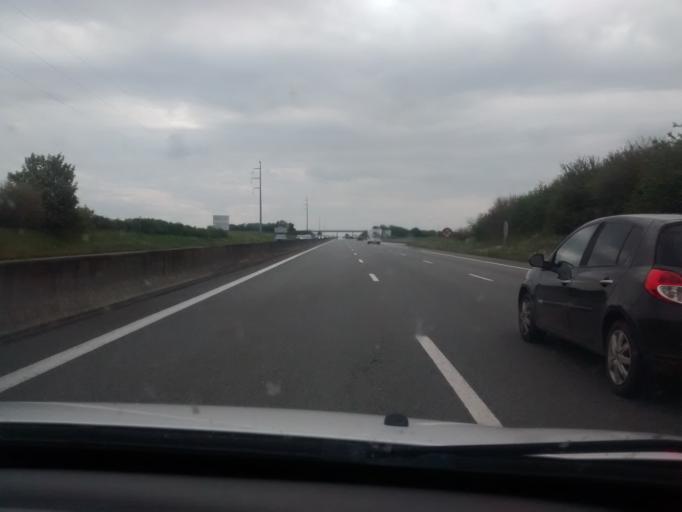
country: FR
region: Centre
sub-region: Departement d'Eure-et-Loir
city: Barjouville
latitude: 48.3714
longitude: 1.4645
